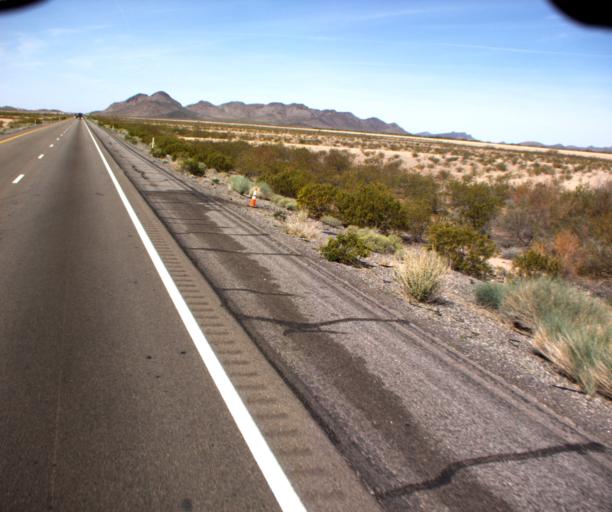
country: US
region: Arizona
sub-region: La Paz County
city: Salome
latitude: 33.6043
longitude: -113.5860
